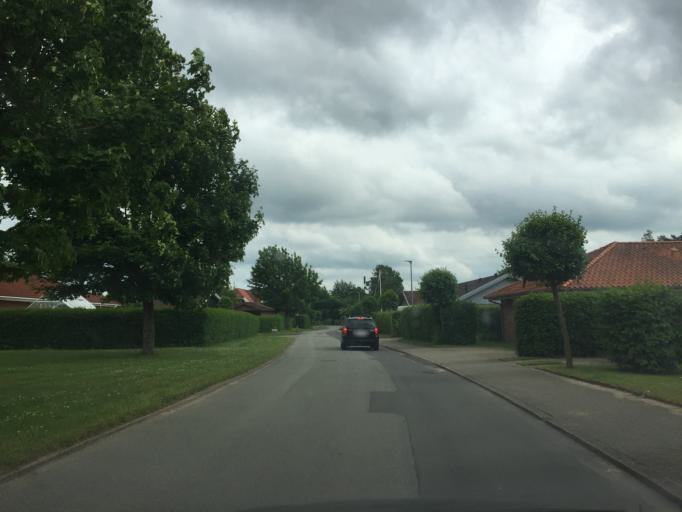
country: DK
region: South Denmark
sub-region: Kolding Kommune
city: Sonder Bjert
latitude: 55.4614
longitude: 9.5603
